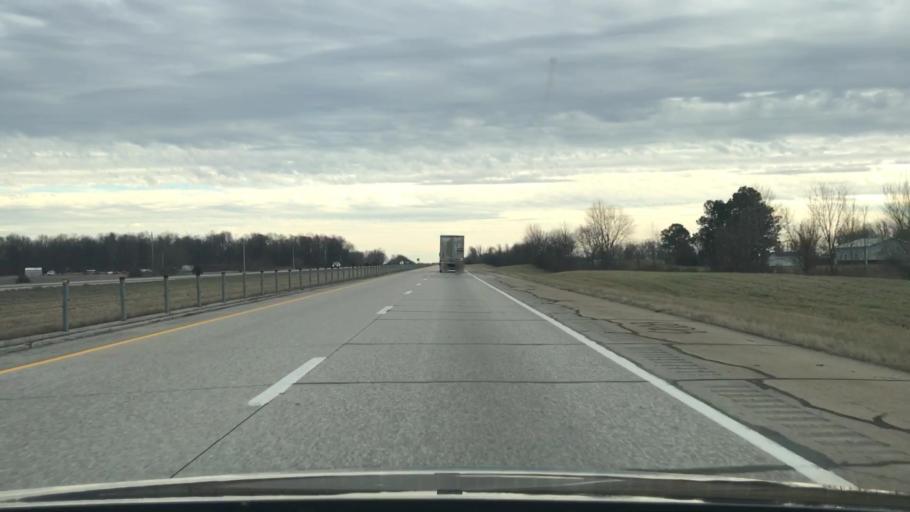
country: US
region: Kentucky
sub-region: Caldwell County
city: Princeton
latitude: 36.9882
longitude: -87.9325
